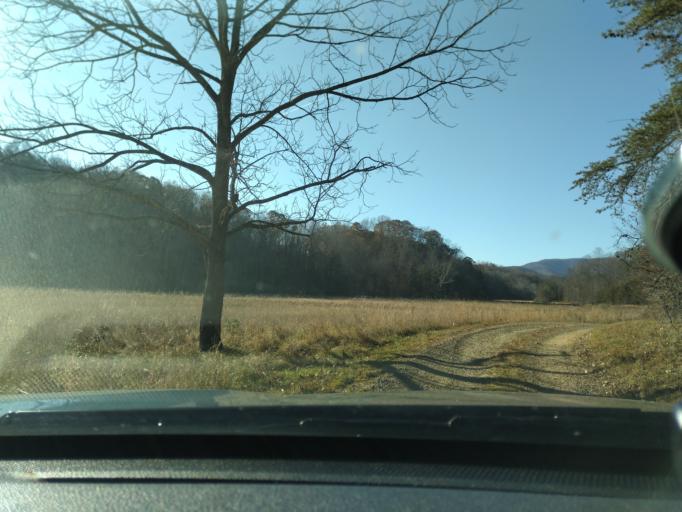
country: US
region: Virginia
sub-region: Floyd County
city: Floyd
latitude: 36.8330
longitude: -80.1793
